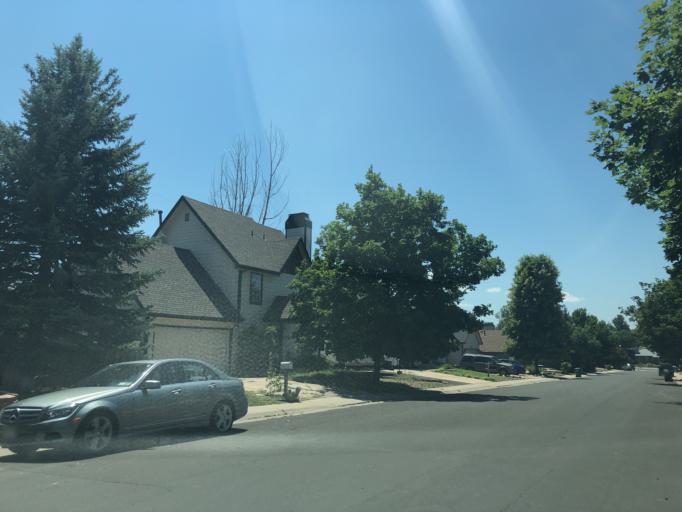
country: US
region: Colorado
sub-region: Arapahoe County
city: Dove Valley
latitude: 39.6246
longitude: -104.7791
